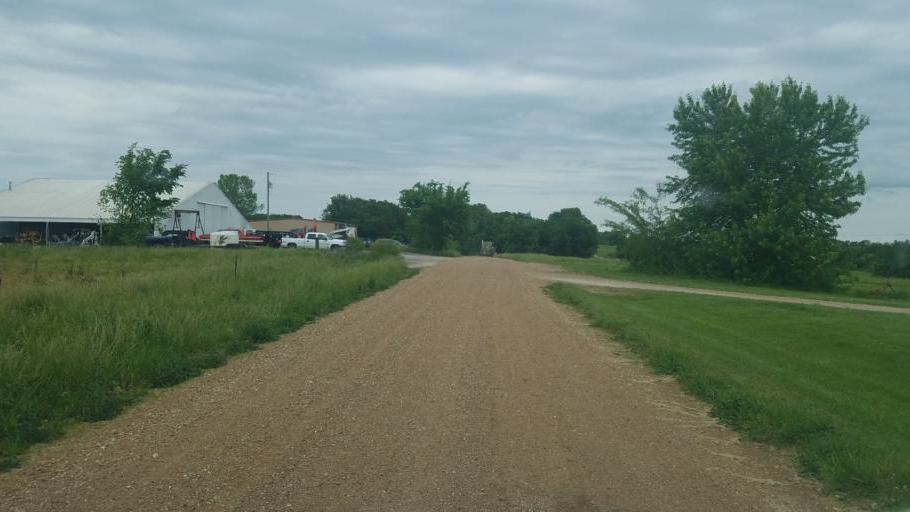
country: US
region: Missouri
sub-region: Moniteau County
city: Tipton
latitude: 38.5642
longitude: -92.7282
